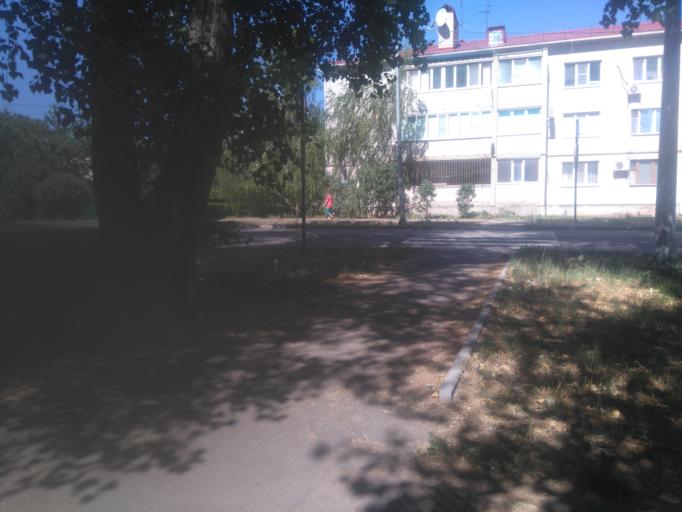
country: RU
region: Krasnodarskiy
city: Fastovetskaya
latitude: 45.9152
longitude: 40.1537
